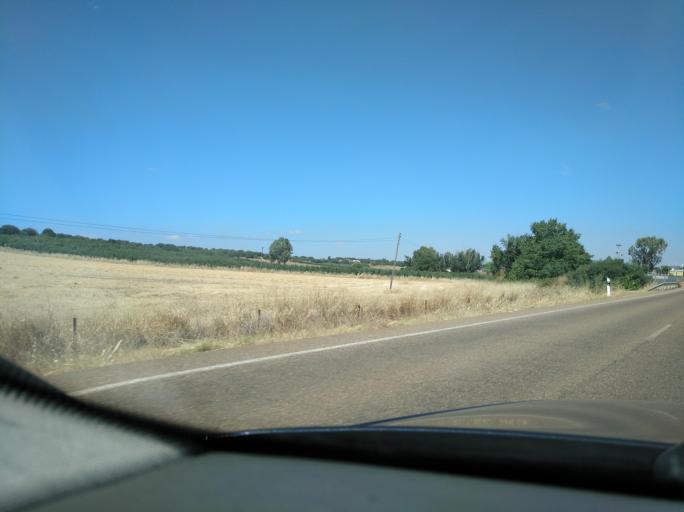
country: ES
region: Extremadura
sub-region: Provincia de Badajoz
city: Olivenza
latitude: 38.7013
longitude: -7.1074
